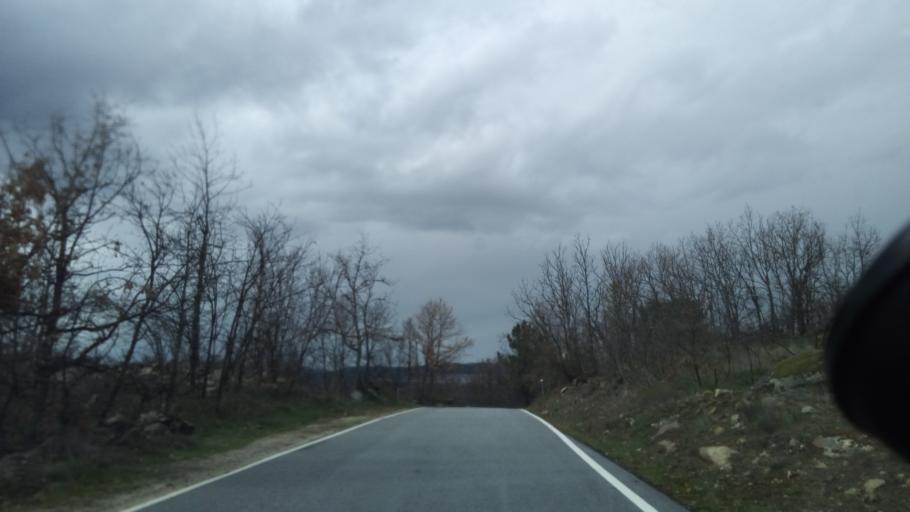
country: PT
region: Guarda
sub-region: Fornos de Algodres
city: Fornos de Algodres
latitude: 40.5846
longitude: -7.4827
